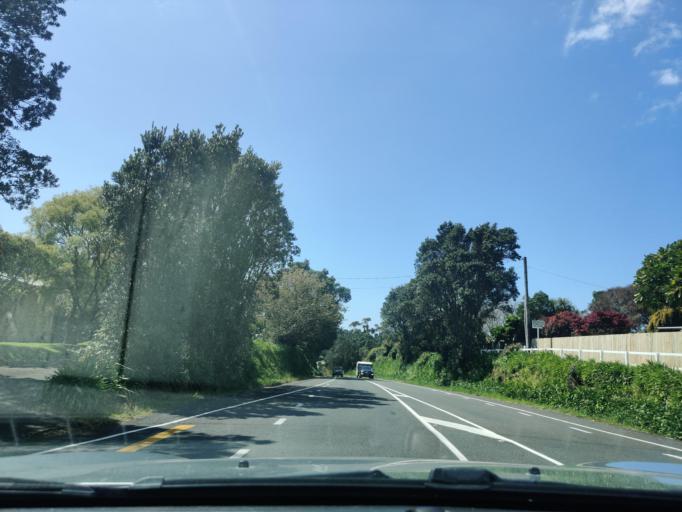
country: NZ
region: Taranaki
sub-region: New Plymouth District
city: New Plymouth
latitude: -39.1153
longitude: 173.9574
